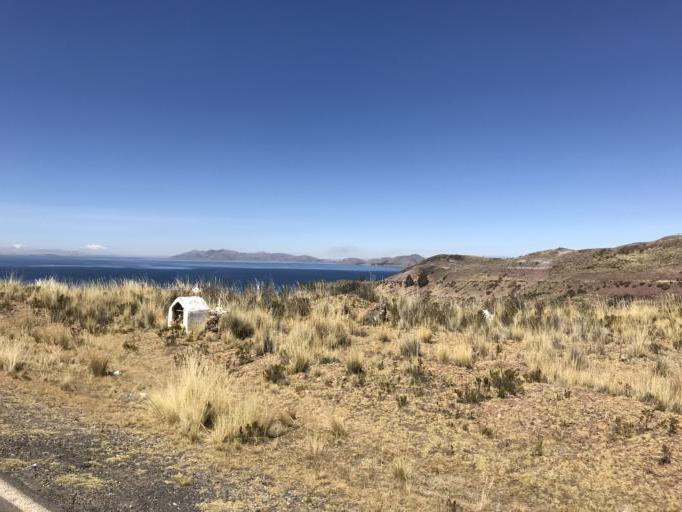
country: BO
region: La Paz
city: San Pablo
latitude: -16.2096
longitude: -68.8397
